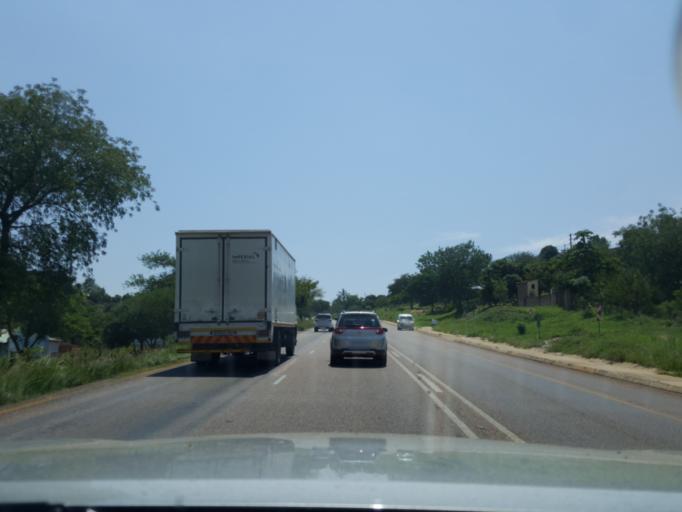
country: ZA
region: Limpopo
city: Thulamahashi
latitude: -24.9739
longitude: 31.1130
